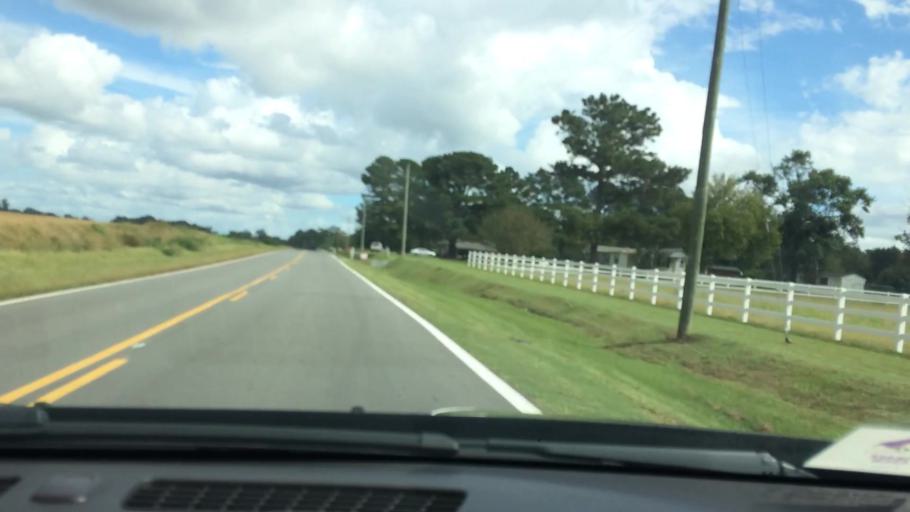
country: US
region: North Carolina
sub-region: Pitt County
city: Ayden
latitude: 35.4556
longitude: -77.4800
